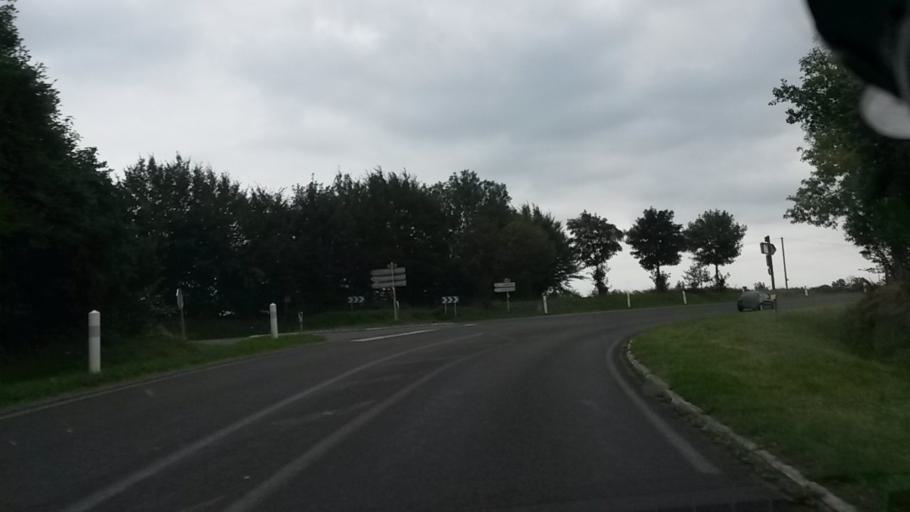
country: FR
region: Haute-Normandie
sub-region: Departement de la Seine-Maritime
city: Gaillefontaine
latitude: 49.6387
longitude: 1.6125
